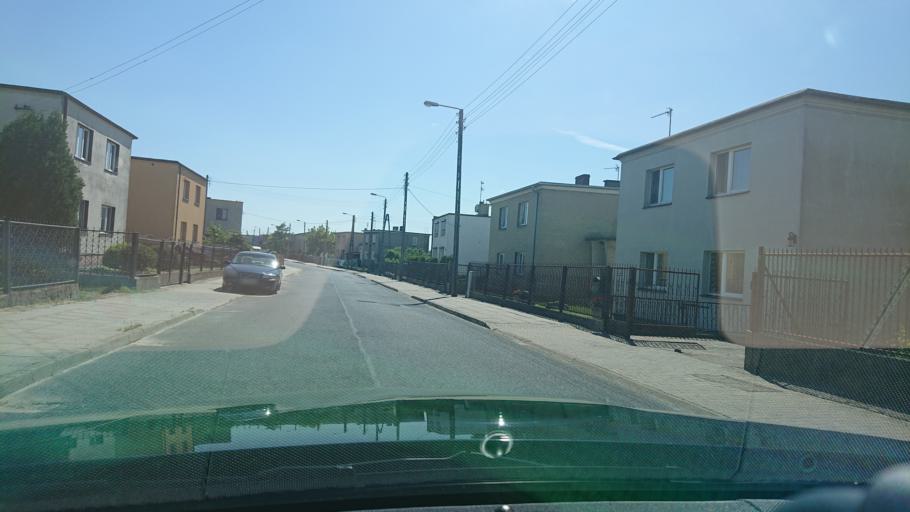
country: PL
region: Greater Poland Voivodeship
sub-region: Powiat gnieznienski
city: Gniezno
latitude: 52.5102
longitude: 17.5899
